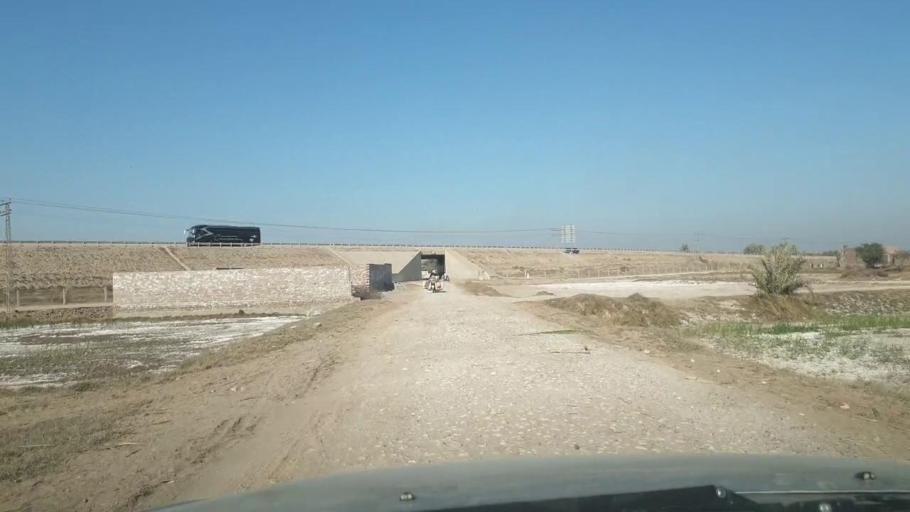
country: PK
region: Sindh
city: Ghotki
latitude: 28.0527
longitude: 69.3382
